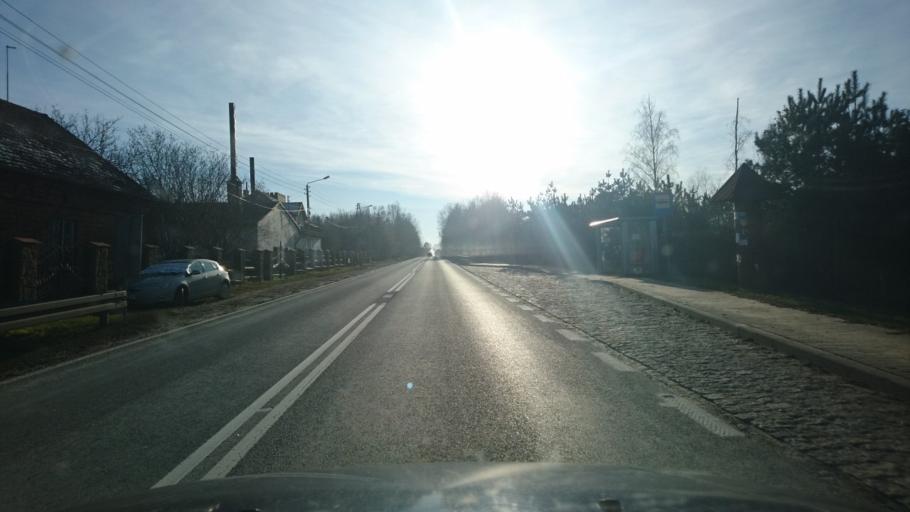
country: PL
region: Opole Voivodeship
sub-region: Powiat oleski
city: Dalachow
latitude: 51.0747
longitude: 18.6024
